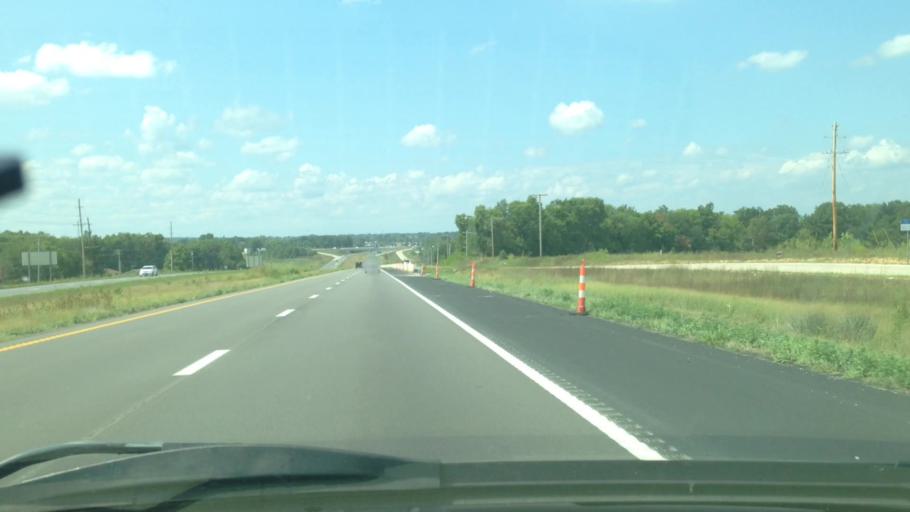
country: US
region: Missouri
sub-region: Lincoln County
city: Moscow Mills
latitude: 38.9583
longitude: -90.9445
